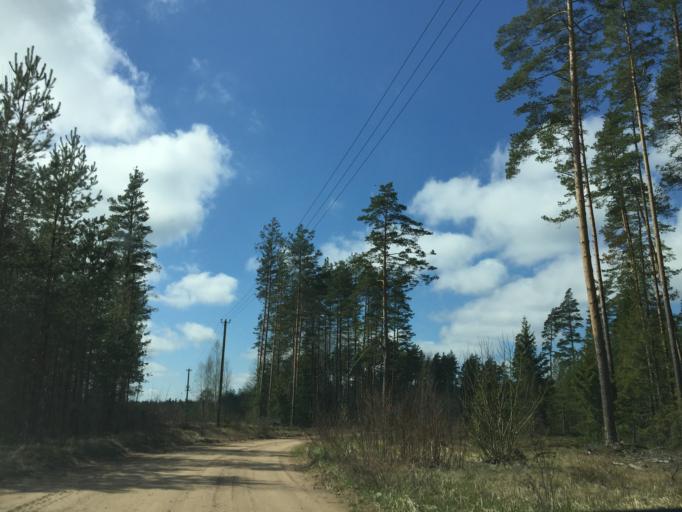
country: EE
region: Valgamaa
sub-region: Valga linn
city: Valga
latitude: 57.6136
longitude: 26.1835
